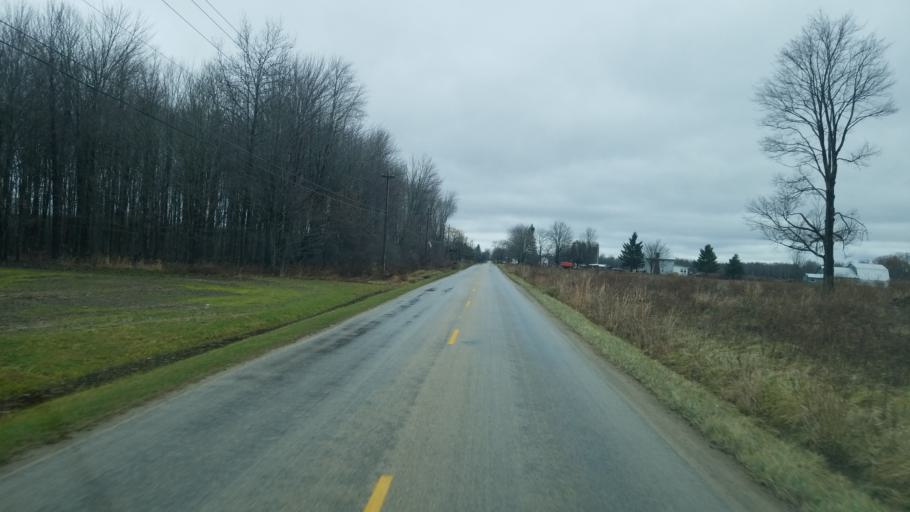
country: US
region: Ohio
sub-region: Ashtabula County
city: North Kingsville
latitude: 41.7756
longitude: -80.6233
